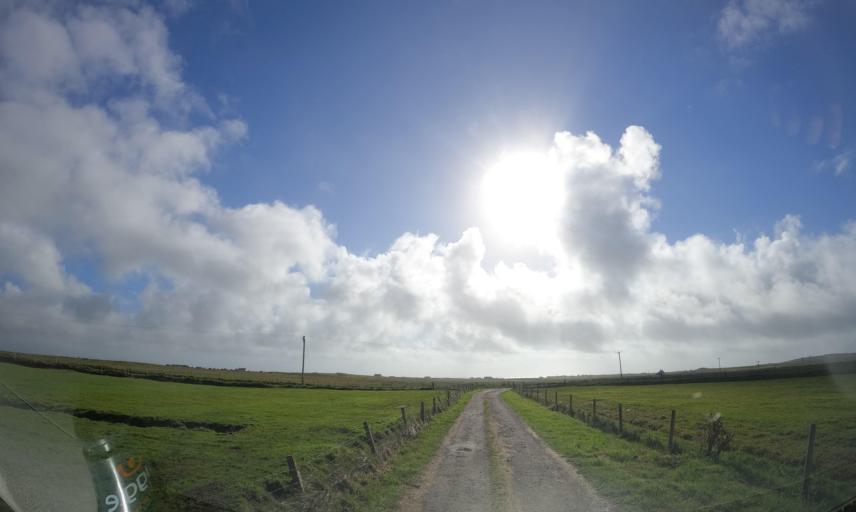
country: GB
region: Scotland
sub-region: Eilean Siar
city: Barra
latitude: 56.4765
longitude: -6.9203
